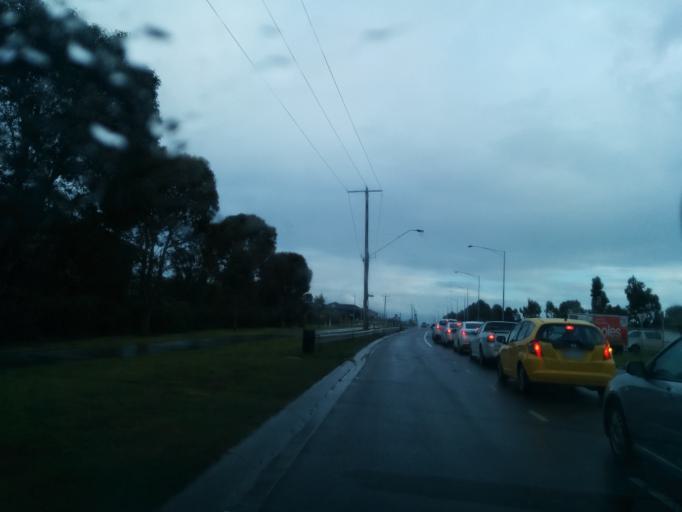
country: AU
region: Victoria
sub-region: Wyndham
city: Point Cook
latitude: -37.8998
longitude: 144.7537
